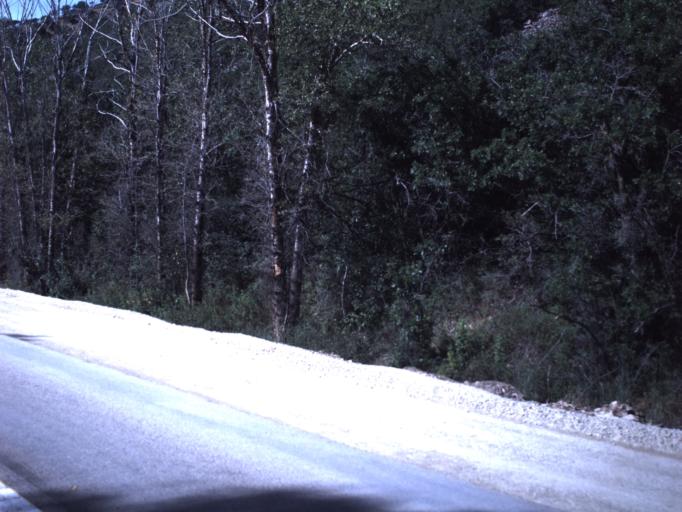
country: US
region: Utah
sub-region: Wasatch County
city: Heber
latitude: 40.3782
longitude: -111.2963
